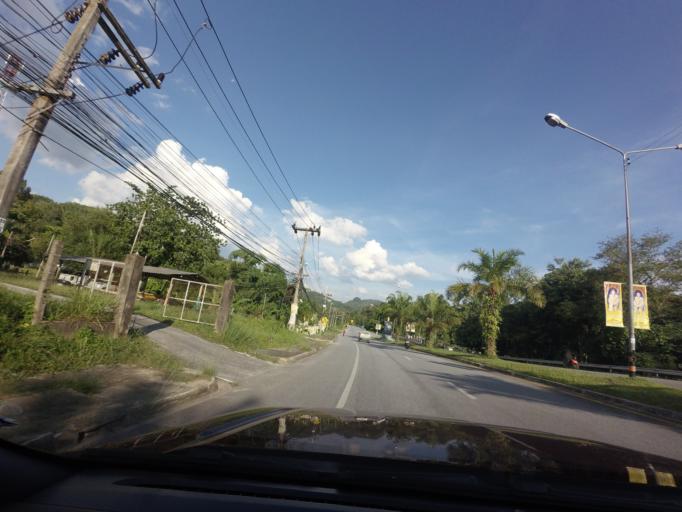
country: TH
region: Yala
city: Than To
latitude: 6.1647
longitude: 101.1822
